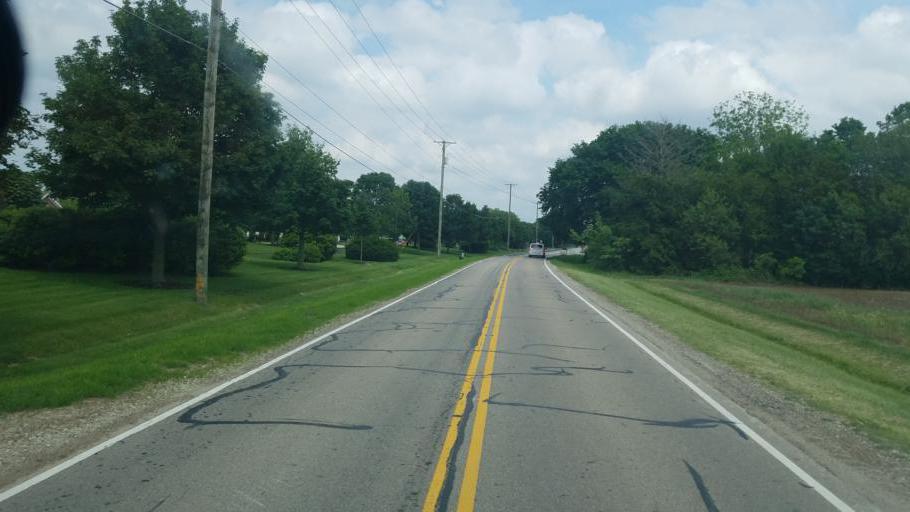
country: US
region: Ohio
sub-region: Franklin County
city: Hilliard
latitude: 40.0773
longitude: -83.1702
